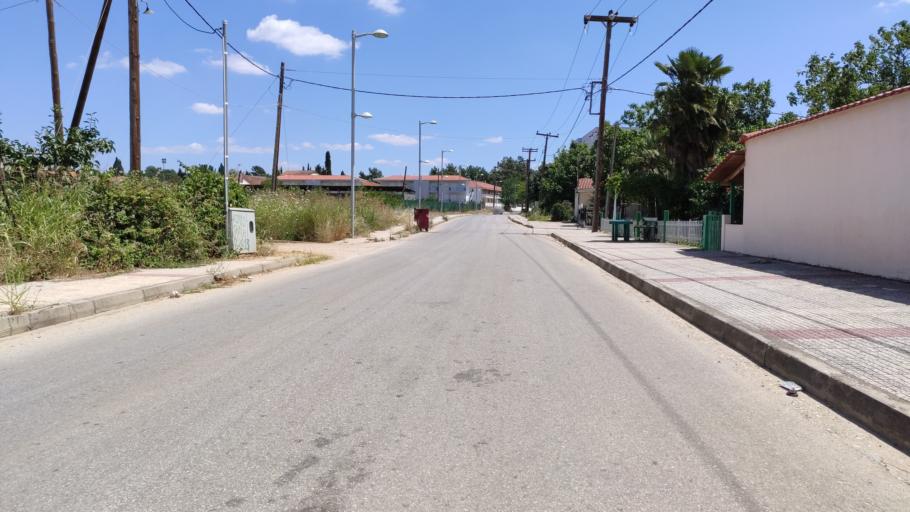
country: GR
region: East Macedonia and Thrace
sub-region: Nomos Rodopis
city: Komotini
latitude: 41.1301
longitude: 25.4059
